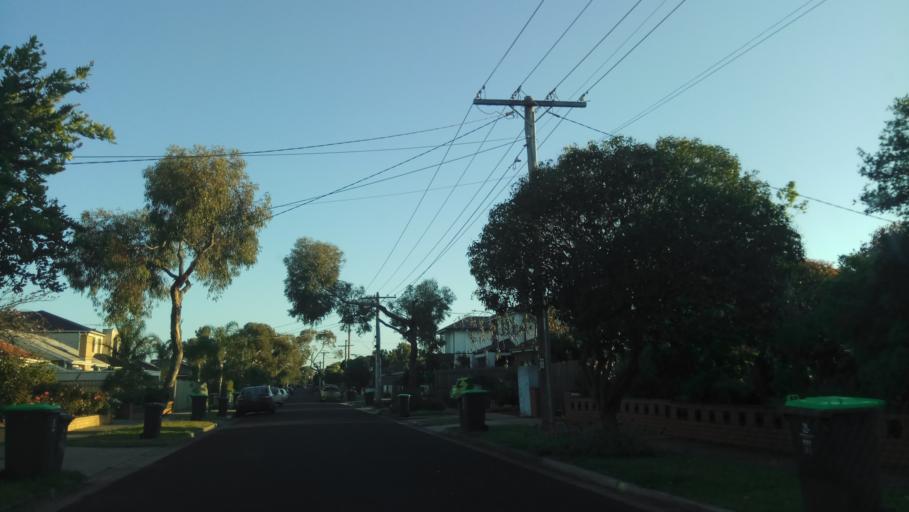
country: AU
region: Victoria
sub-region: Hobsons Bay
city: Altona
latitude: -37.8690
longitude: 144.8133
